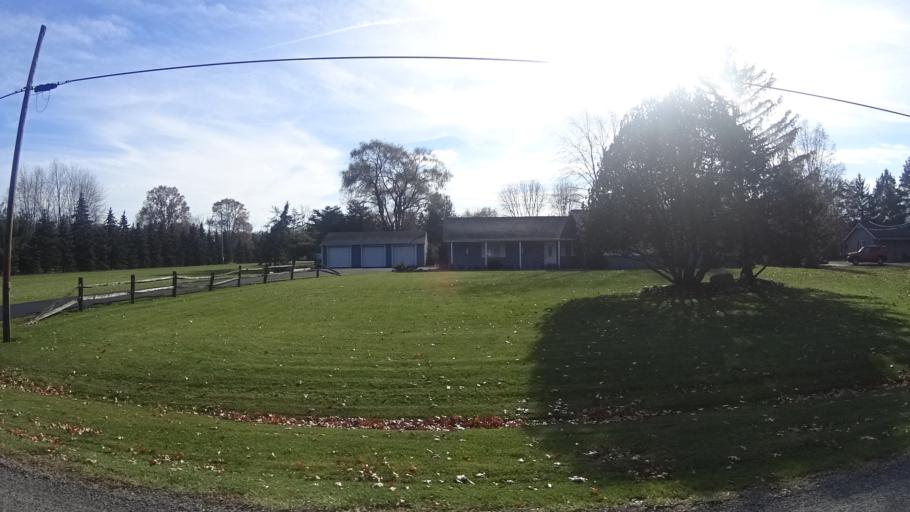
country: US
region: Ohio
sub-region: Lorain County
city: Eaton Estates
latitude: 41.2943
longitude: -81.9861
